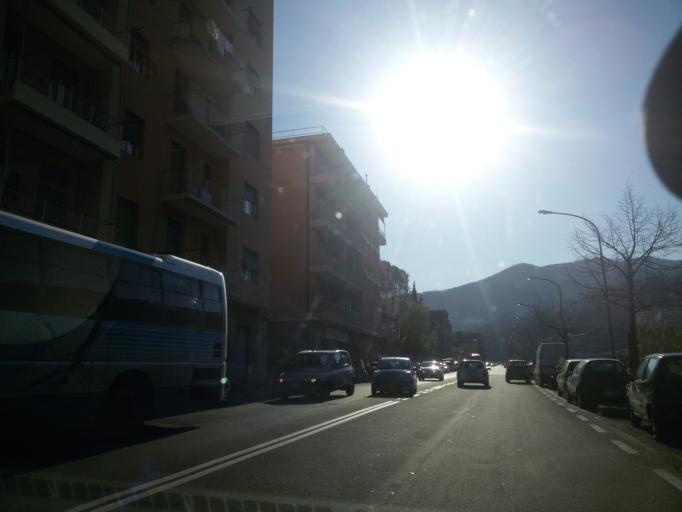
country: IT
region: Liguria
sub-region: Provincia di Genova
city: Piccarello
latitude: 44.4495
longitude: 8.9946
